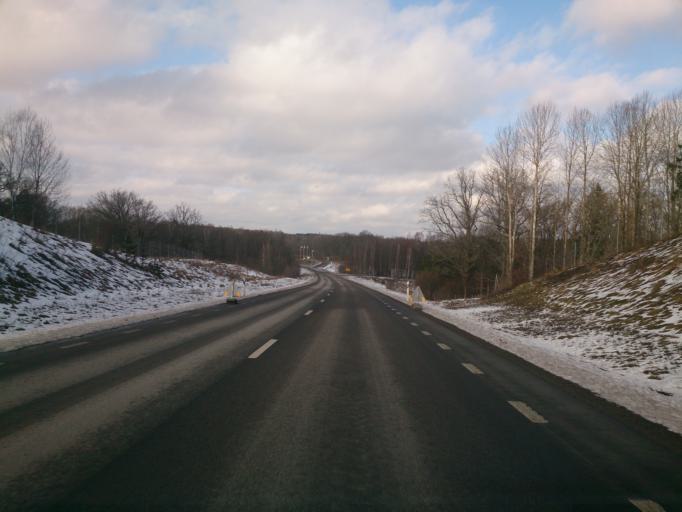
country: SE
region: OEstergoetland
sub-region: Atvidabergs Kommun
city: Atvidaberg
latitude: 58.1912
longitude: 16.0229
